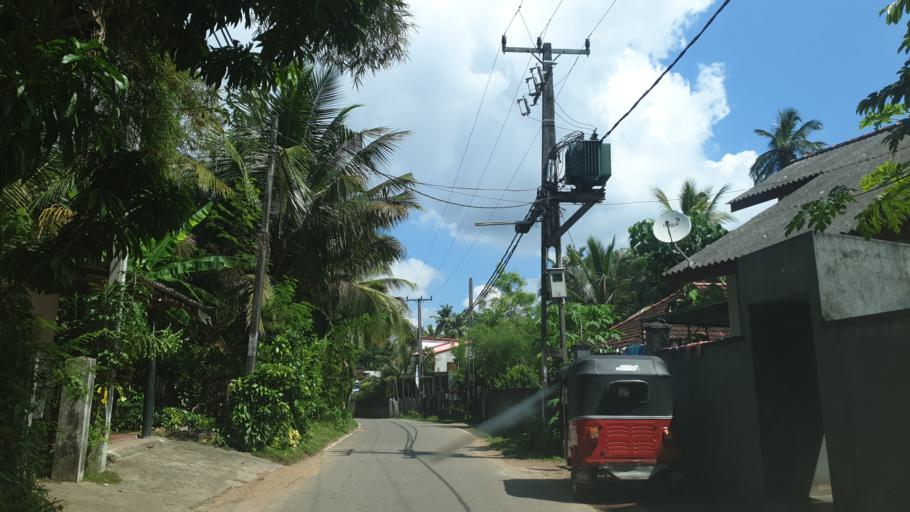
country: LK
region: Western
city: Panadura
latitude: 6.6812
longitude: 79.9410
